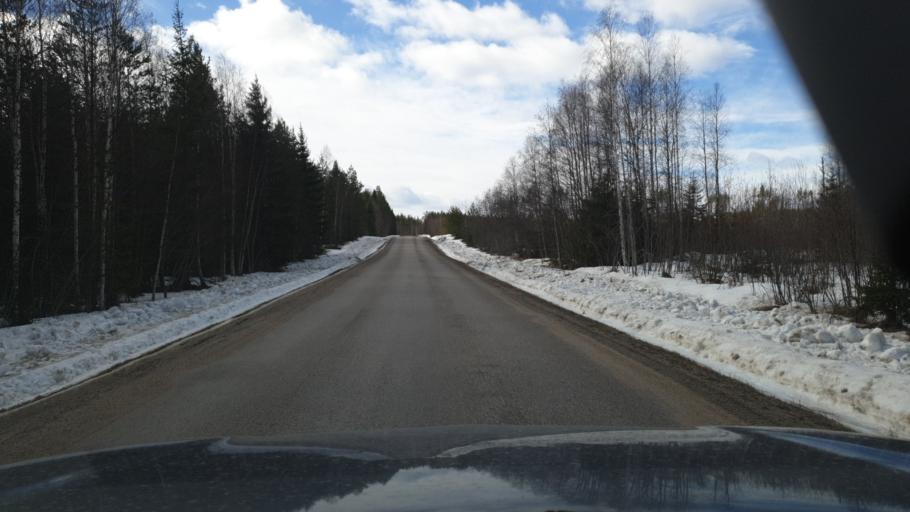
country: SE
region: Gaevleborg
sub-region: Ljusdals Kommun
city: Farila
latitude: 61.8451
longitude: 15.9391
